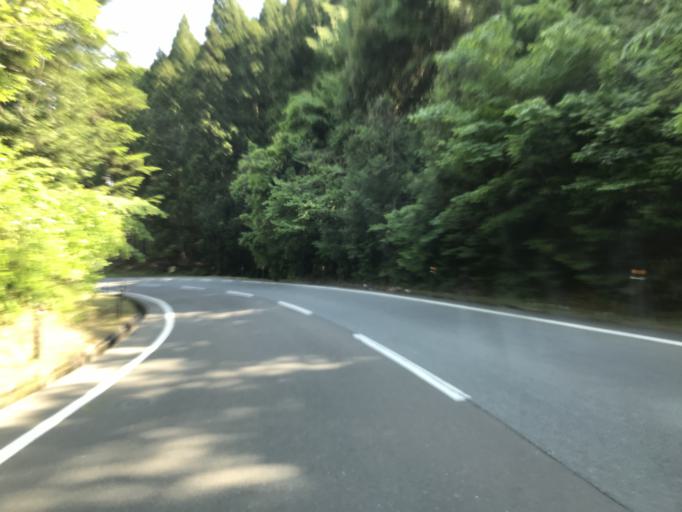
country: JP
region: Miyagi
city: Marumori
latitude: 37.7933
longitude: 140.8822
